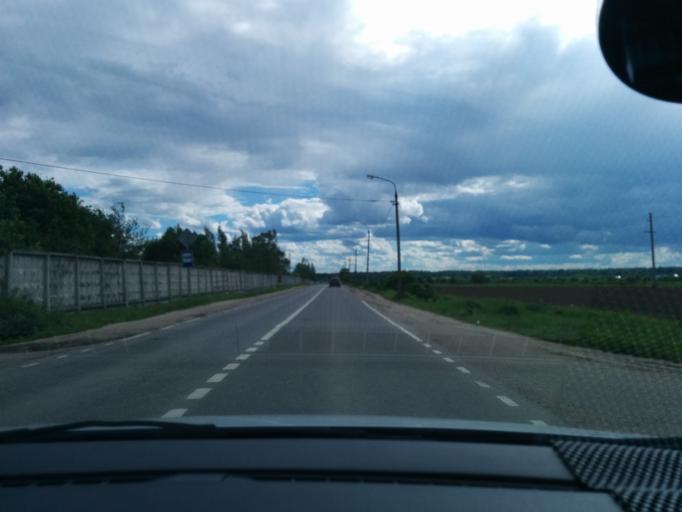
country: RU
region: Moskovskaya
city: Lugovaya
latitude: 56.0474
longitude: 37.4767
